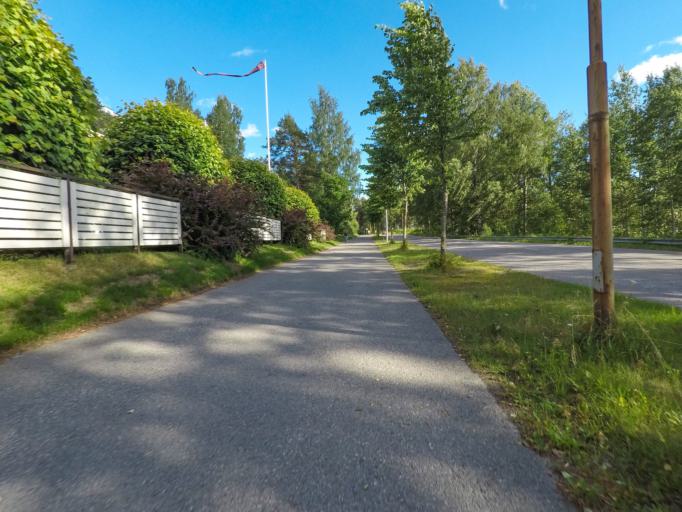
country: FI
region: South Karelia
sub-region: Lappeenranta
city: Lappeenranta
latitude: 61.0674
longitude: 28.1572
